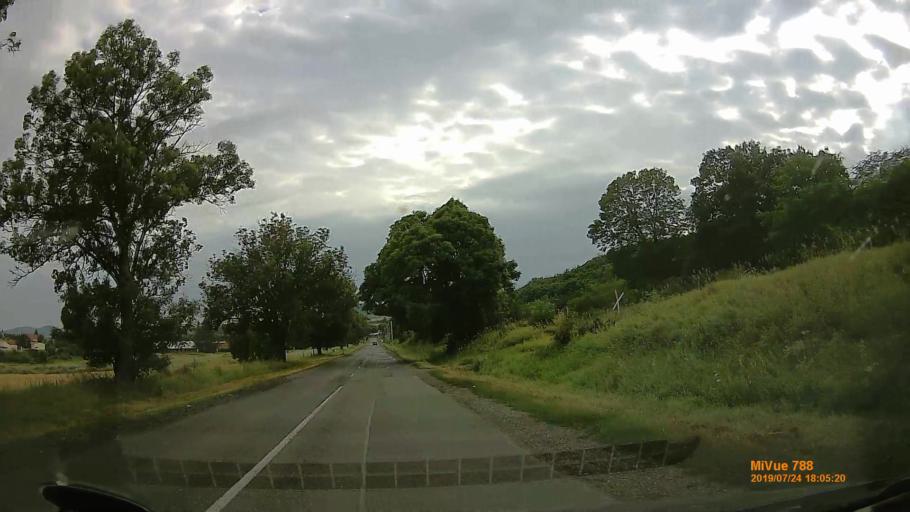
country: HU
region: Borsod-Abauj-Zemplen
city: Abaujszanto
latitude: 48.2913
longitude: 21.1882
